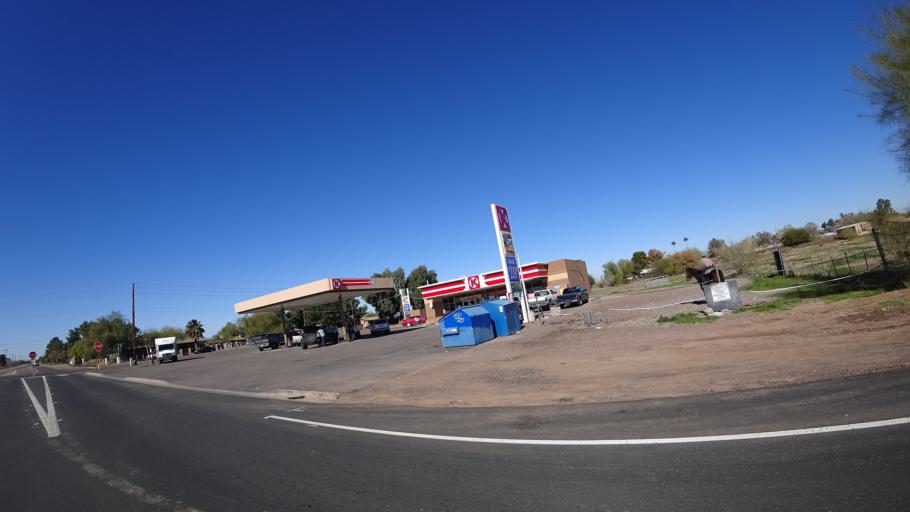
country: US
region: Arizona
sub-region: Maricopa County
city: Avondale
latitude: 33.3918
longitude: -112.3054
